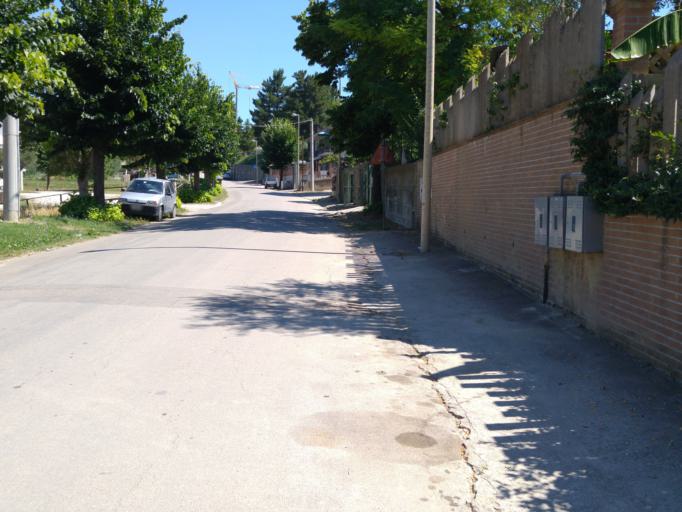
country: IT
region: Abruzzo
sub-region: Provincia di Pescara
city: Elice
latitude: 42.5229
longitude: 13.9701
